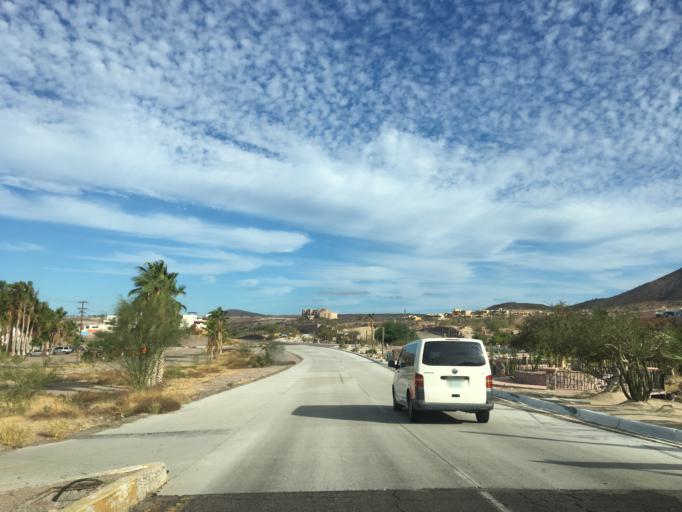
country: MX
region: Baja California Sur
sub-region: La Paz
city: La Paz
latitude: 24.2025
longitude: -110.2982
